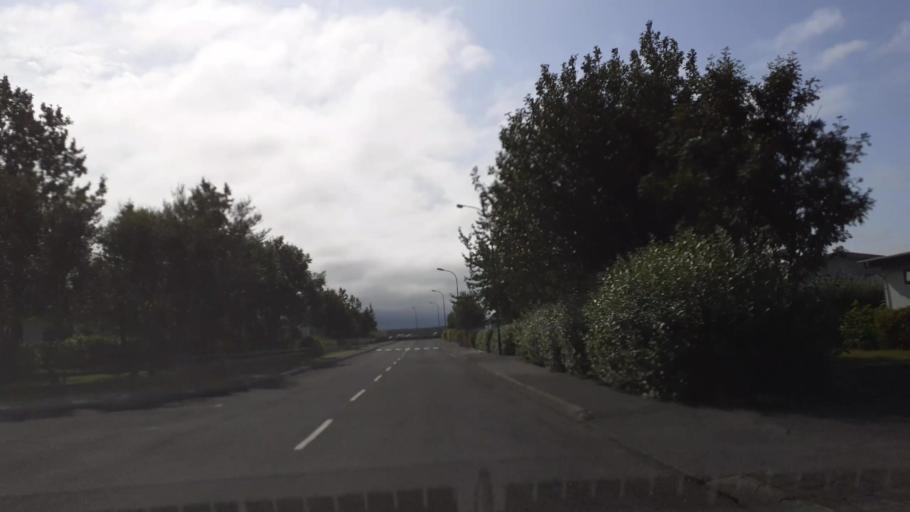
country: IS
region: Northwest
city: Saudarkrokur
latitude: 65.6622
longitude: -20.2803
